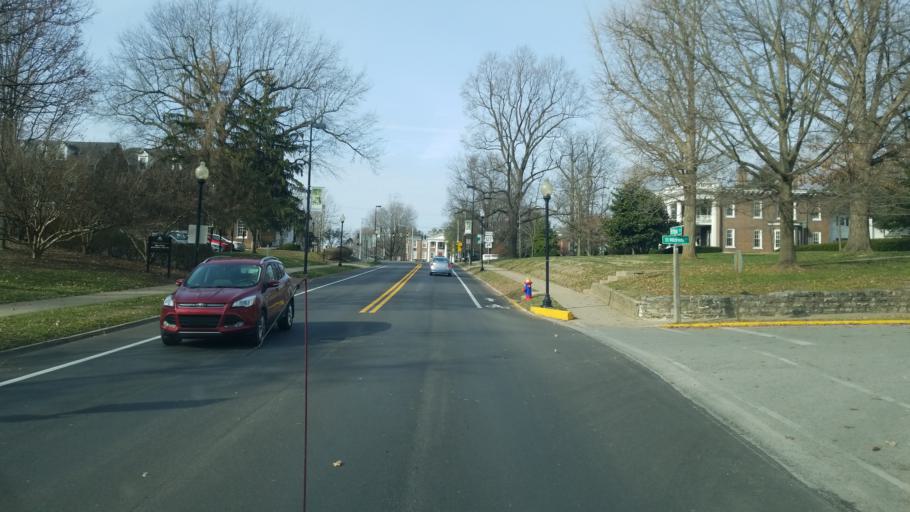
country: US
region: Kentucky
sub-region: Boyle County
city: Danville
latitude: 37.6463
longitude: -84.7805
